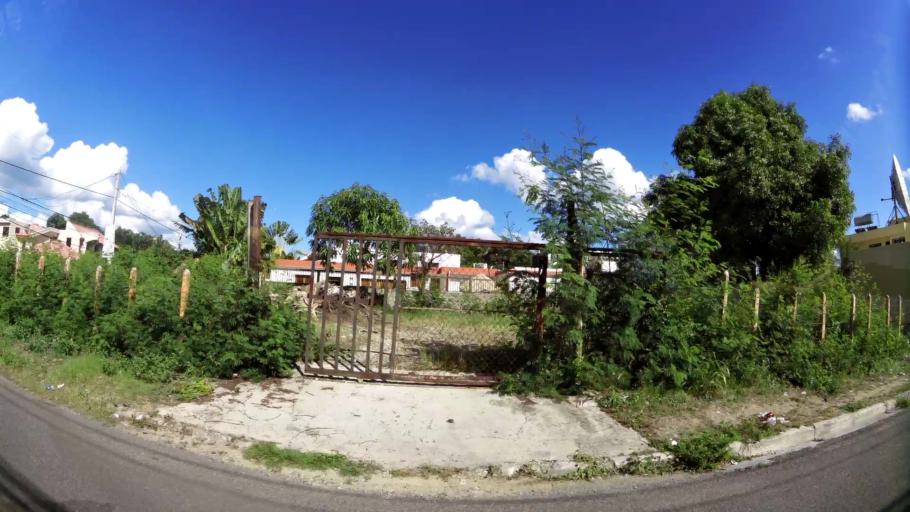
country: DO
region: Santiago
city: Santiago de los Caballeros
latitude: 19.4490
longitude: -70.6710
